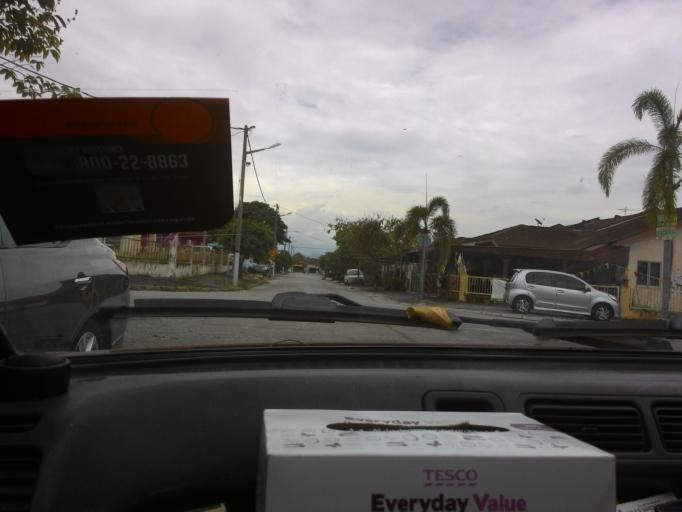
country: MY
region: Perak
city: Ipoh
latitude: 4.6782
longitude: 101.0814
